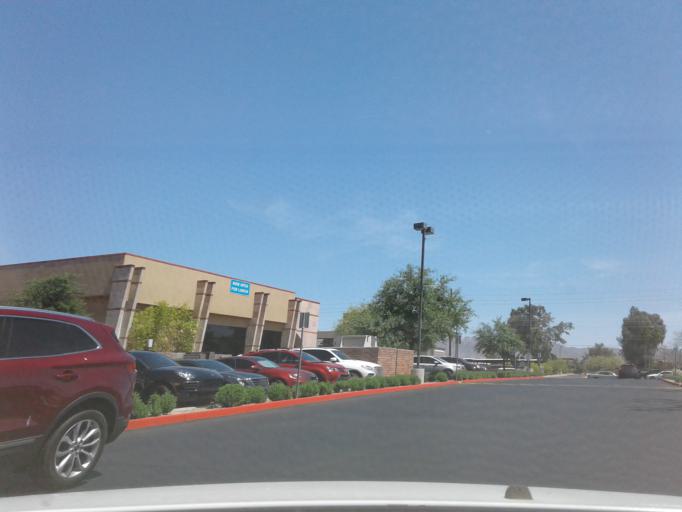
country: US
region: Arizona
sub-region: Maricopa County
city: Paradise Valley
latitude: 33.6160
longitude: -111.9268
